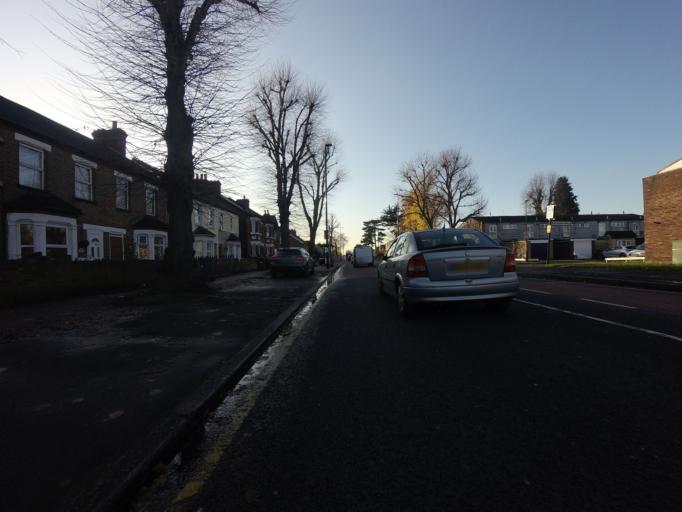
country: GB
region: England
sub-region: Greater London
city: Feltham
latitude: 51.4559
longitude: -0.4181
